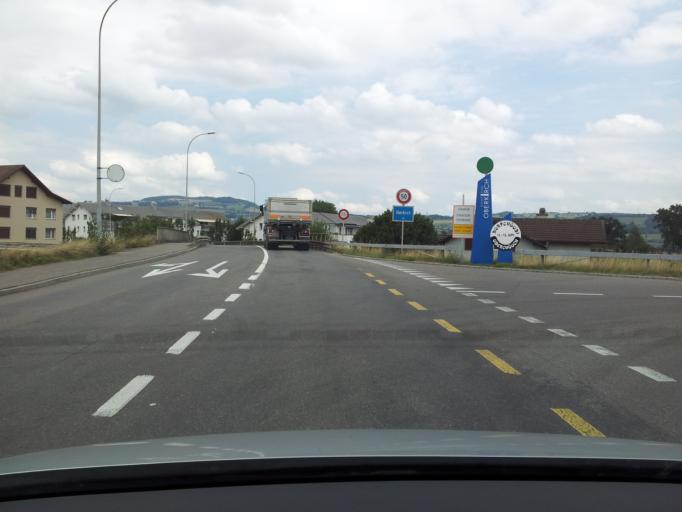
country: CH
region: Lucerne
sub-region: Sursee District
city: Oberkirch
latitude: 47.1532
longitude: 8.1156
